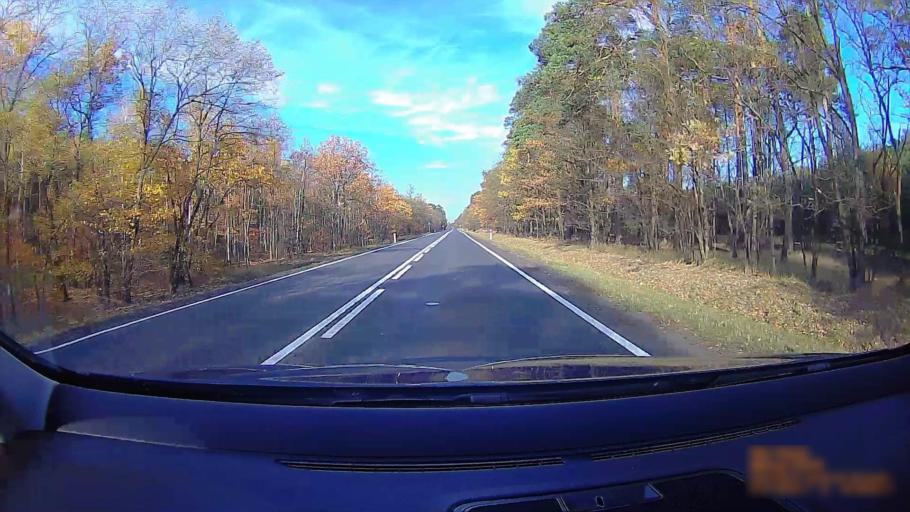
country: PL
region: Greater Poland Voivodeship
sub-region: Powiat kaliski
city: Stawiszyn
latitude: 51.9903
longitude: 18.1403
